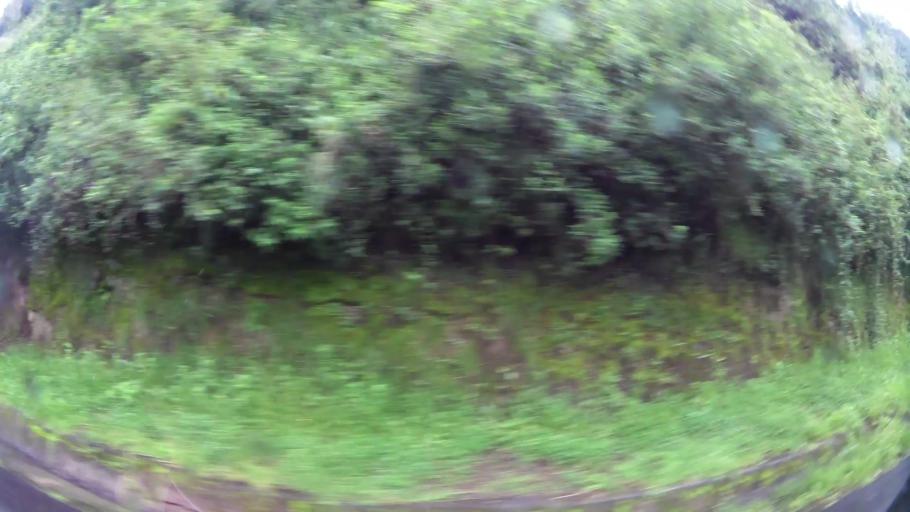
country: EC
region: Pichincha
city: Sangolqui
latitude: -0.2708
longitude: -78.4475
